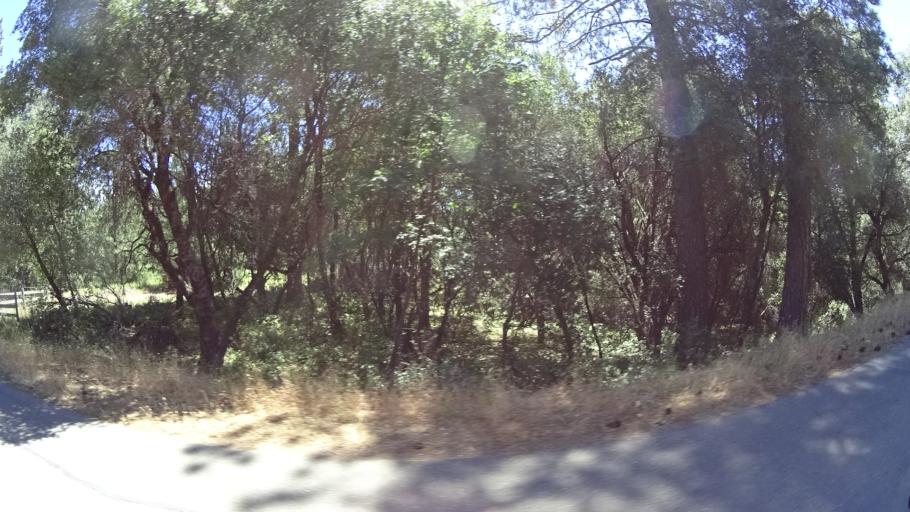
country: US
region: California
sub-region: Amador County
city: Pioneer
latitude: 38.3753
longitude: -120.5189
